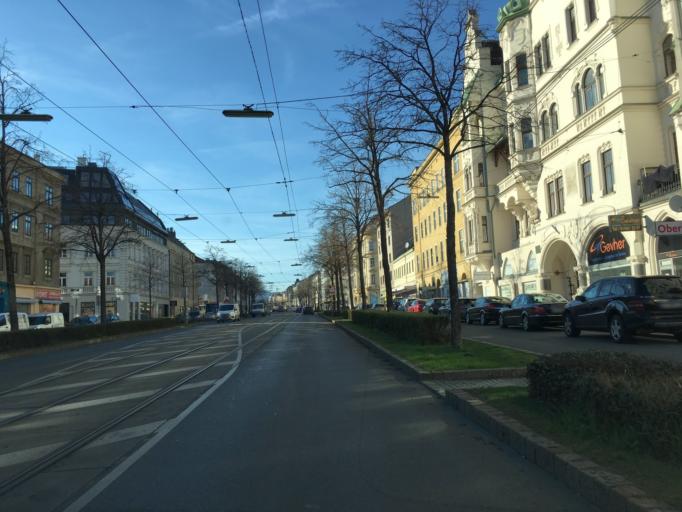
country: AT
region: Vienna
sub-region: Wien Stadt
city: Vienna
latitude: 48.2201
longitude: 16.3251
